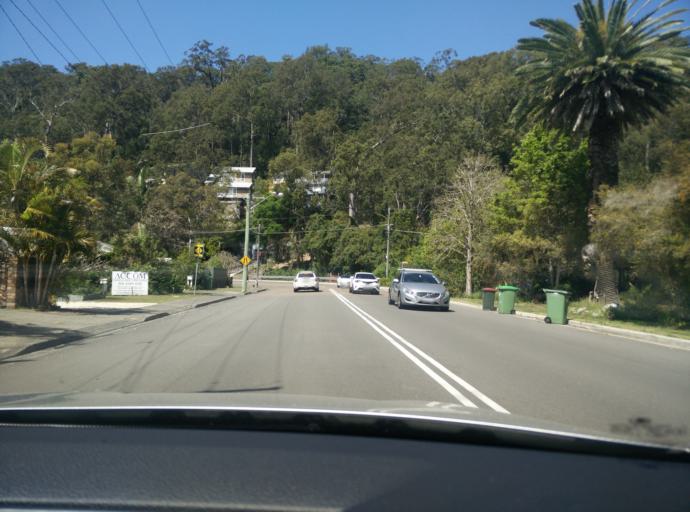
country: AU
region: New South Wales
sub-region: Gosford Shire
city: Umina
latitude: -33.5341
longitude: 151.3081
